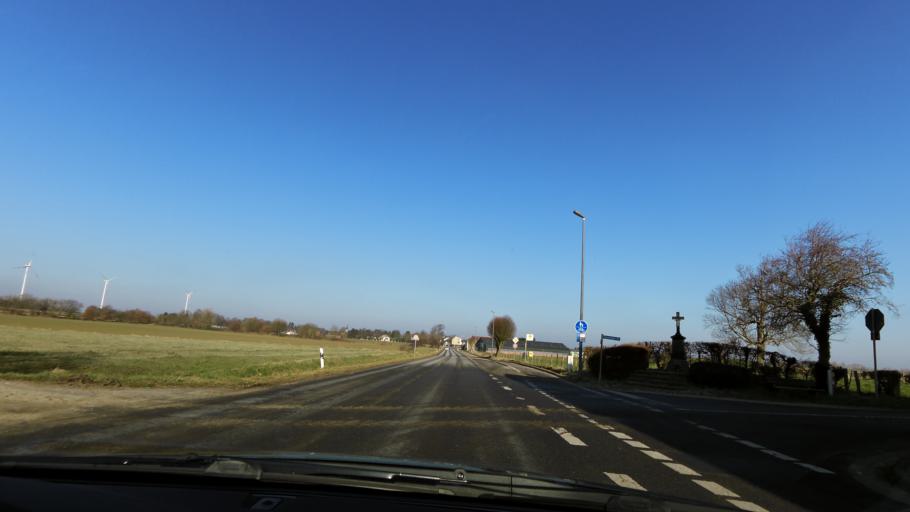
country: NL
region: Limburg
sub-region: Gemeente Kerkrade
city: Kerkrade
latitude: 50.8269
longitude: 6.0513
